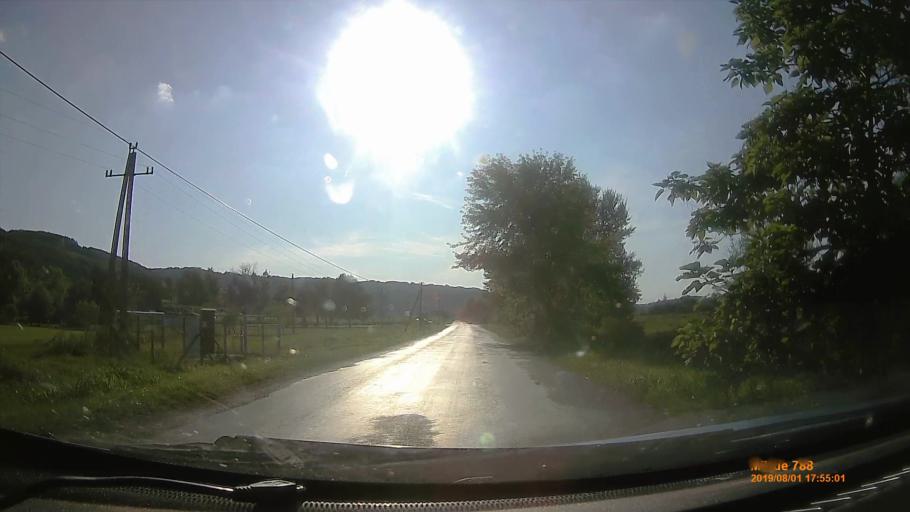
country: HU
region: Baranya
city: Sasd
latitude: 46.1932
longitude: 18.1427
